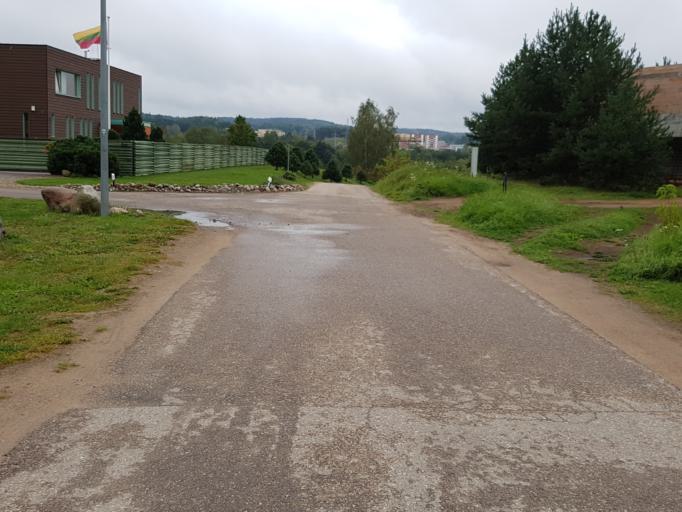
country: LT
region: Vilnius County
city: Lazdynai
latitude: 54.6519
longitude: 25.2081
